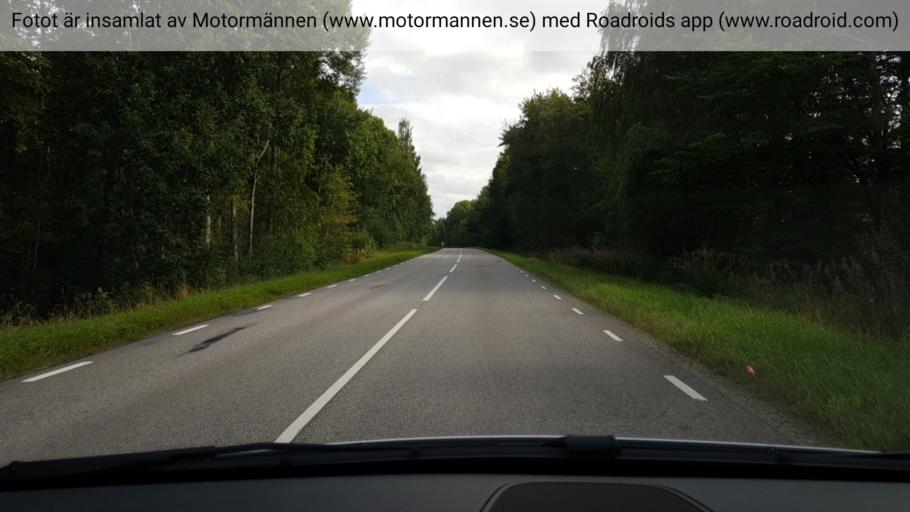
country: SE
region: Vaestra Goetaland
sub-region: Essunga Kommun
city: Nossebro
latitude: 58.1850
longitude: 12.7365
